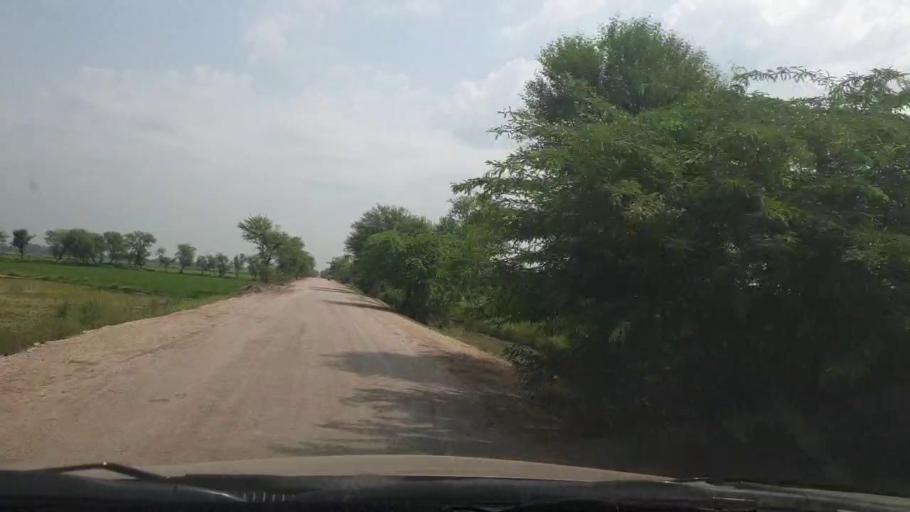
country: PK
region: Sindh
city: Miro Khan
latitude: 27.6848
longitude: 68.1897
